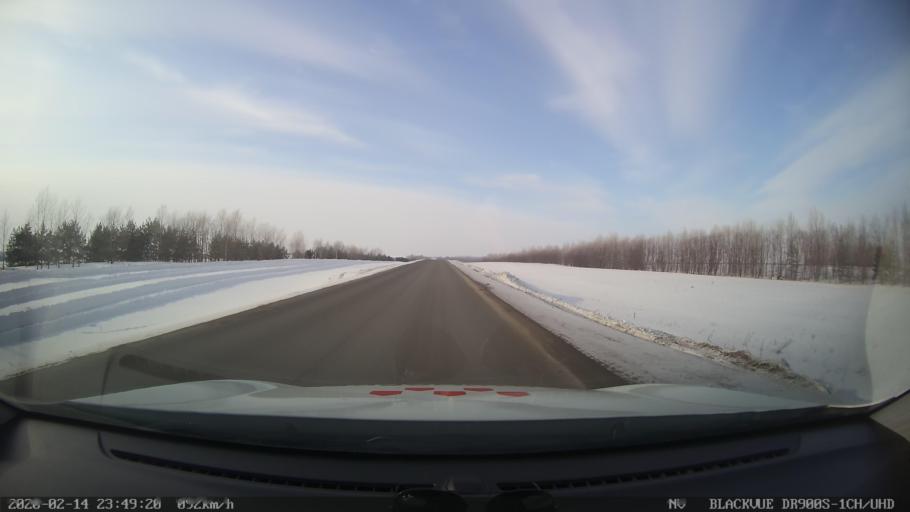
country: RU
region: Tatarstan
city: Kuybyshevskiy Zaton
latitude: 55.2529
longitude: 49.1846
